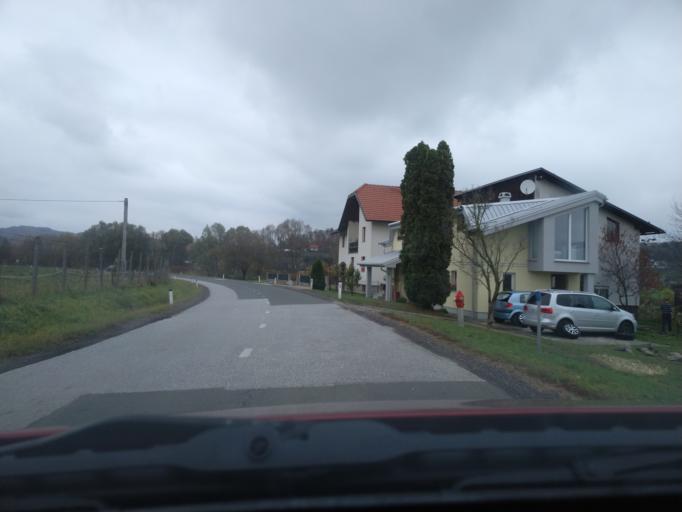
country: SI
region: Pesnica
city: Pesnica pri Mariboru
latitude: 46.6007
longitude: 15.6558
